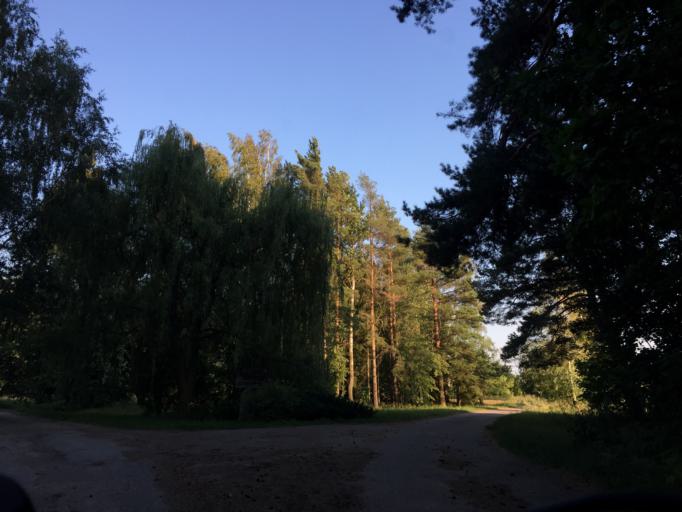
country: LV
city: Tervete
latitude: 56.4711
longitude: 23.3722
